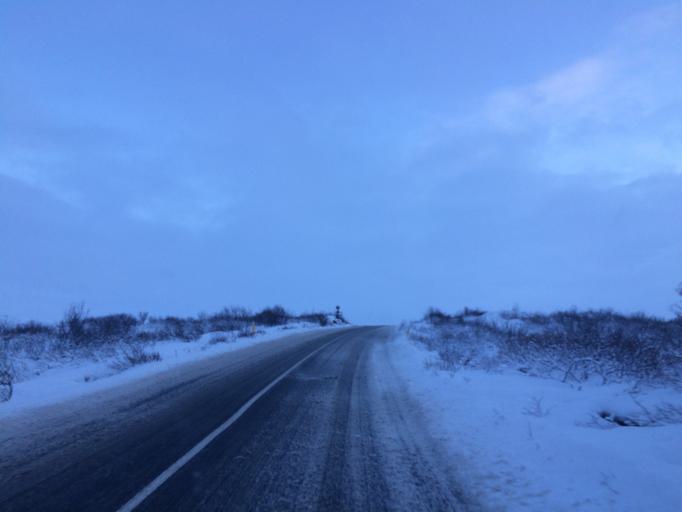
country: IS
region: South
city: Hveragerdi
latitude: 64.2323
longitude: -21.0363
